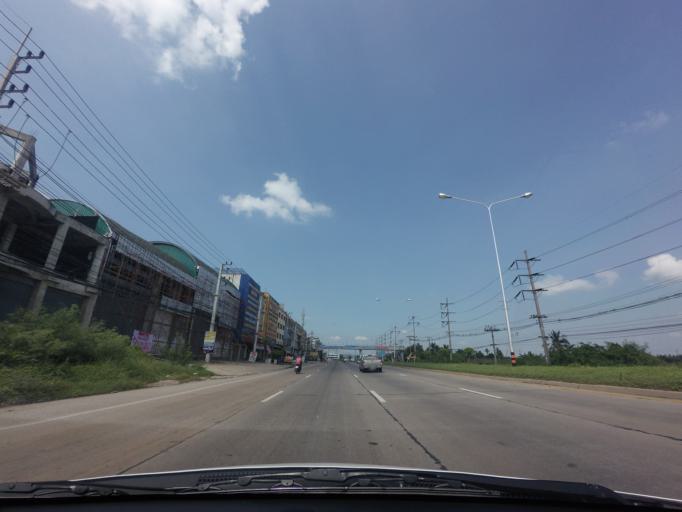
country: TH
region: Nakhon Pathom
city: Sam Phran
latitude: 13.7553
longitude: 100.1919
